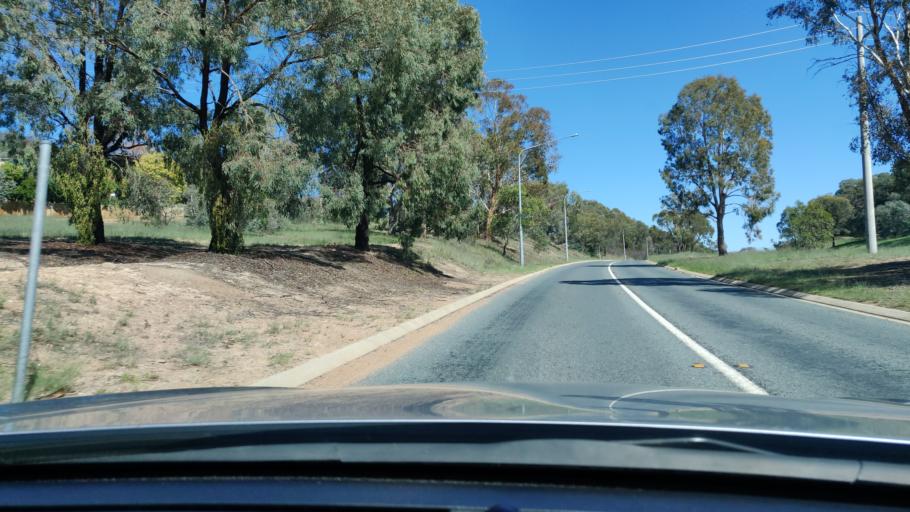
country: AU
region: Australian Capital Territory
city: Macarthur
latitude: -35.4454
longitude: 149.1134
